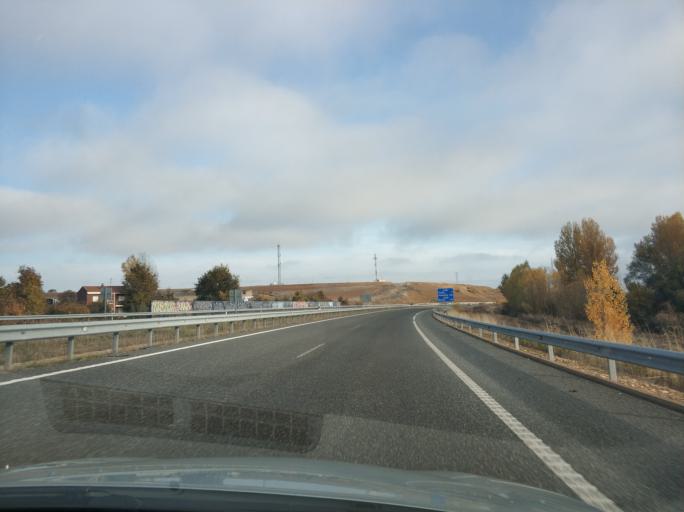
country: ES
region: Castille and Leon
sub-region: Provincia de Leon
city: Valdefresno
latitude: 42.5633
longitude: -5.4808
